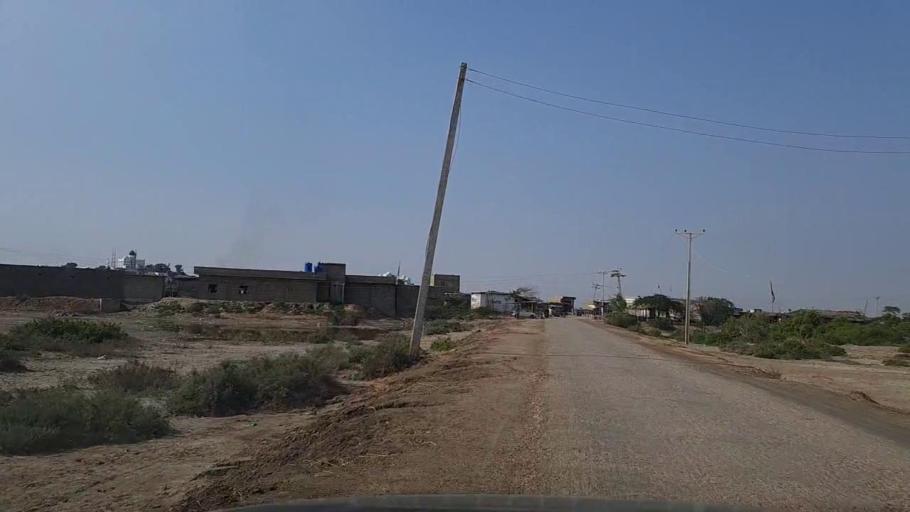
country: PK
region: Sindh
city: Thatta
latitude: 24.5582
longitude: 67.8853
